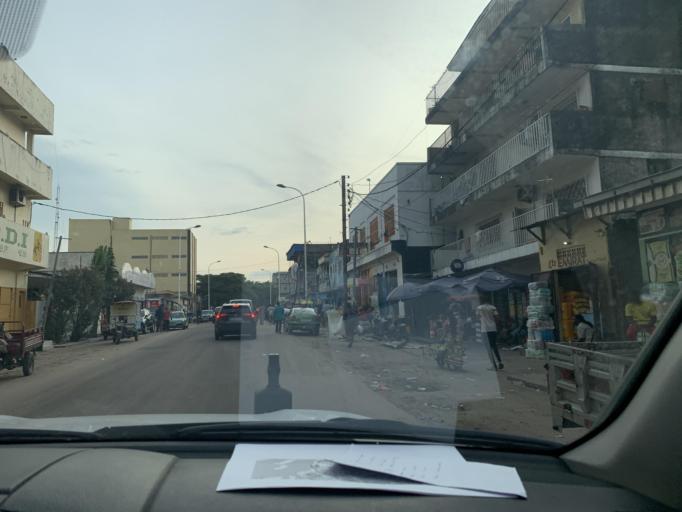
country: CG
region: Brazzaville
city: Brazzaville
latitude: -4.2648
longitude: 15.2872
